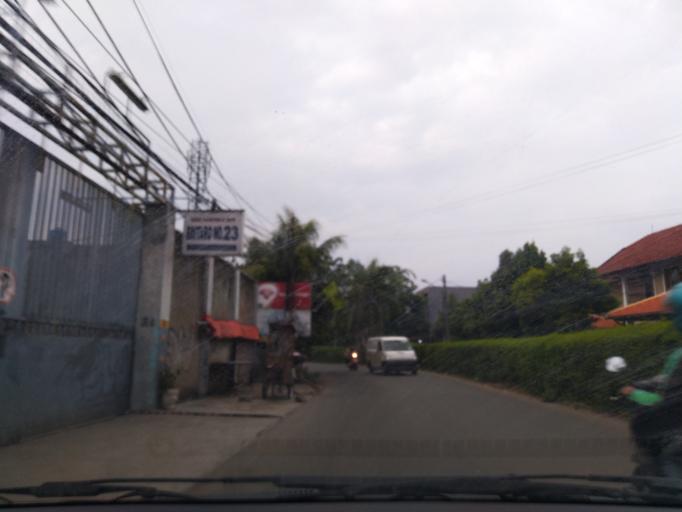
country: ID
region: Banten
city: South Tangerang
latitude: -6.2657
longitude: 106.7446
